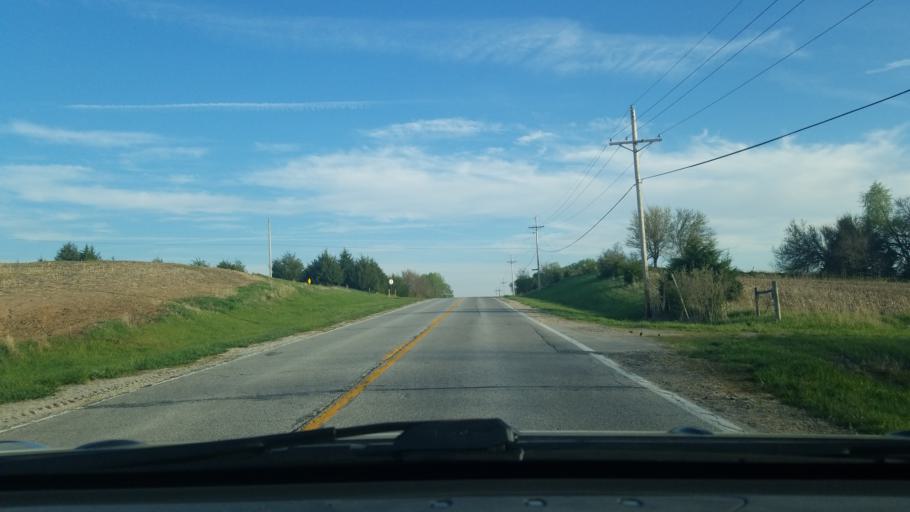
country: US
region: Nebraska
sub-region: Sarpy County
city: Offutt Air Force Base
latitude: 41.0794
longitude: -95.9665
